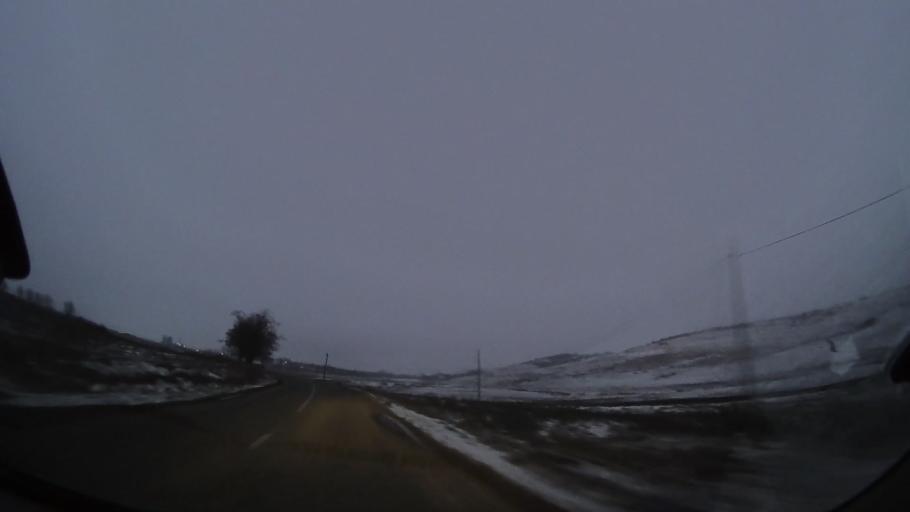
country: RO
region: Vaslui
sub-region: Comuna Dimitrie Cantemir
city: Dimitrie Cantemir
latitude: 46.4917
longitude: 28.0544
